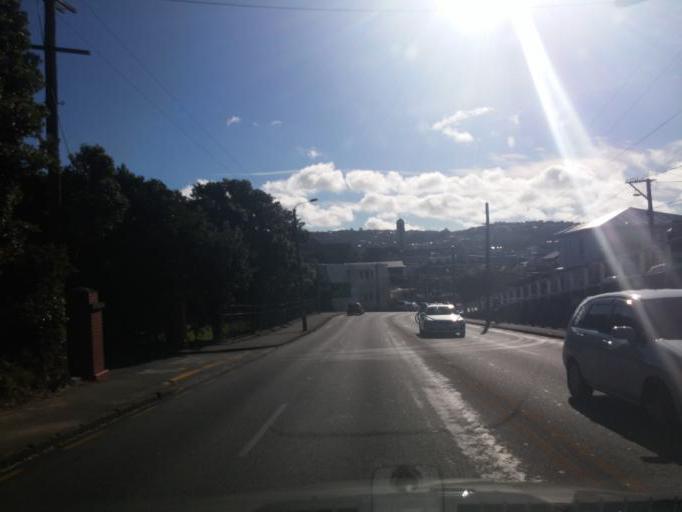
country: NZ
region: Wellington
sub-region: Wellington City
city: Wellington
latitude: -41.3015
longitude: 174.7837
